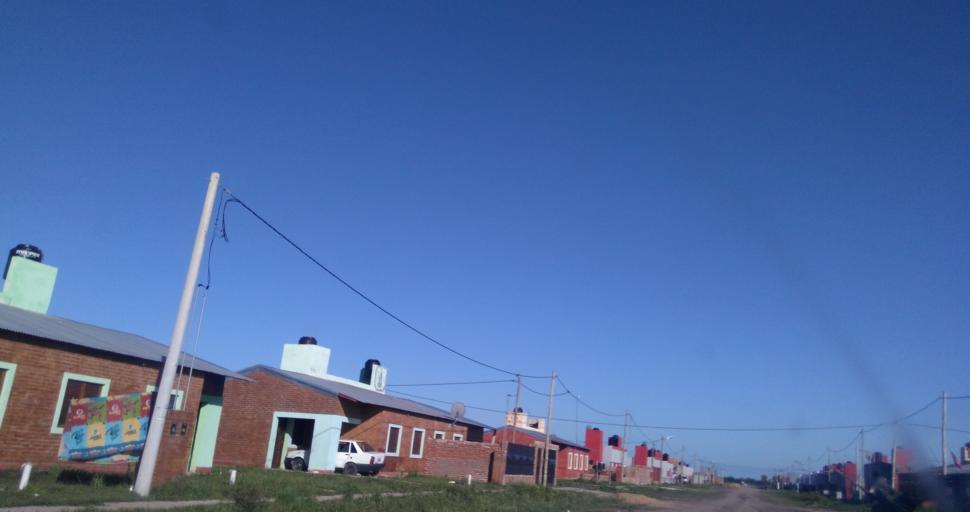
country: AR
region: Chaco
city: Resistencia
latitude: -27.4853
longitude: -59.0105
